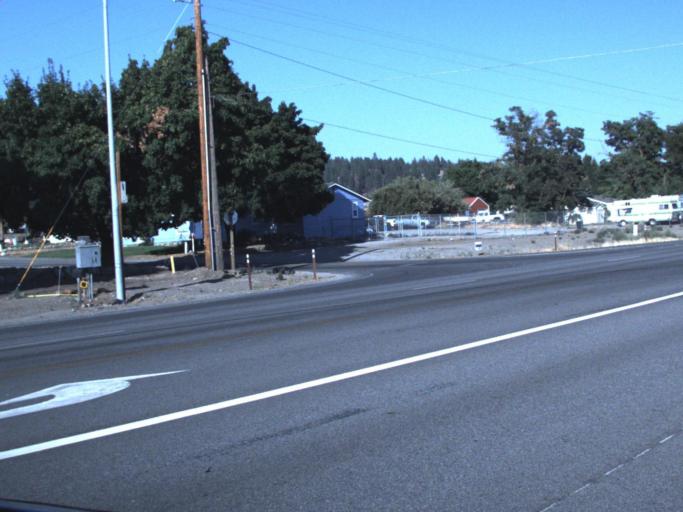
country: US
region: Washington
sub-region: Spokane County
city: Trentwood
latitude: 47.6967
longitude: -117.1758
